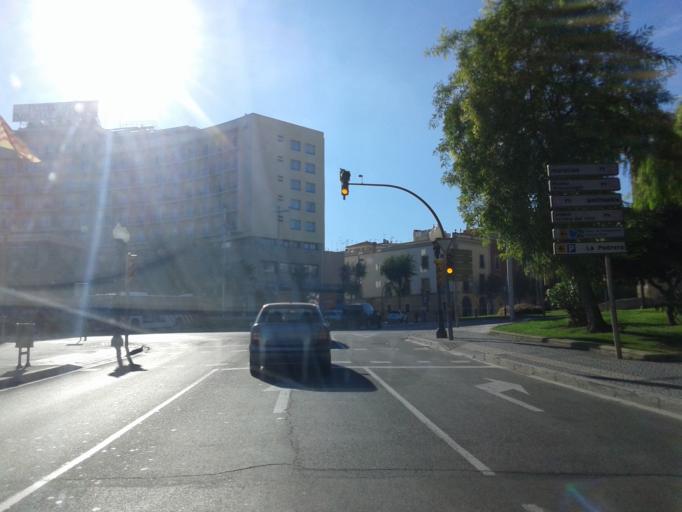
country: ES
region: Catalonia
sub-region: Provincia de Tarragona
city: Tarragona
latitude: 41.1156
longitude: 1.2580
